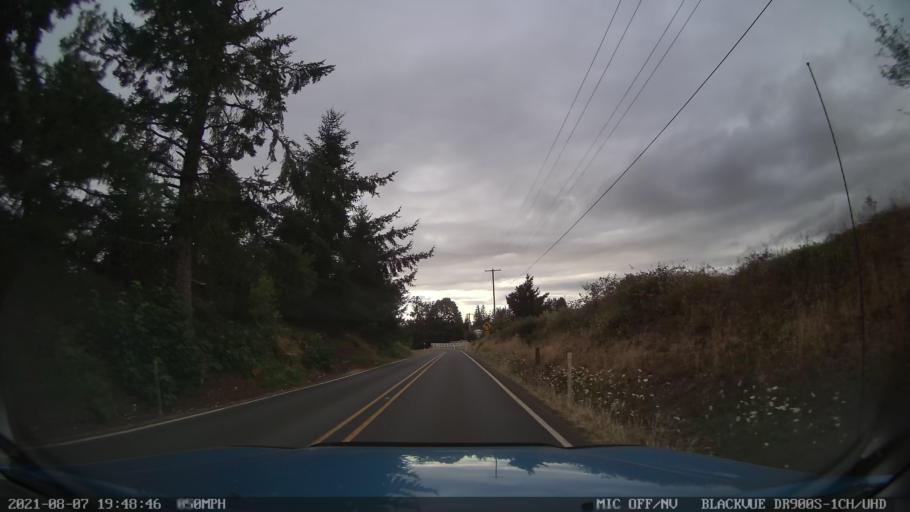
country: US
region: Oregon
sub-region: Marion County
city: Silverton
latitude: 44.9781
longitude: -122.7173
